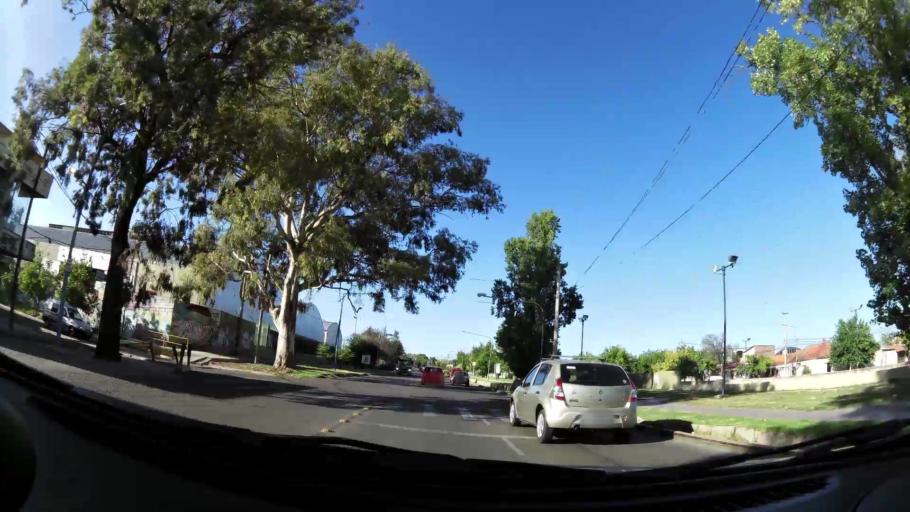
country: AR
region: Mendoza
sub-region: Departamento de Godoy Cruz
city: Godoy Cruz
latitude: -32.9352
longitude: -68.8403
